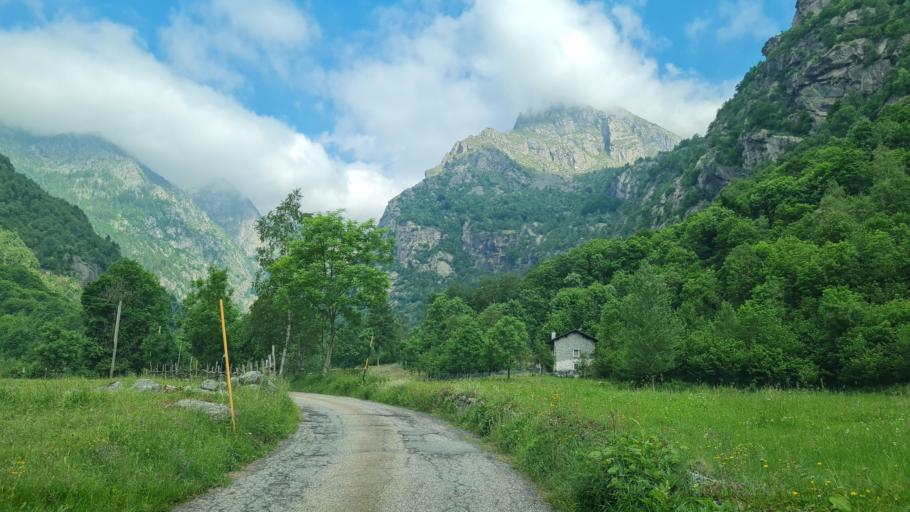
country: IT
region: Piedmont
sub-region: Provincia di Torino
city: Locana
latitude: 45.4509
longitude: 7.4038
